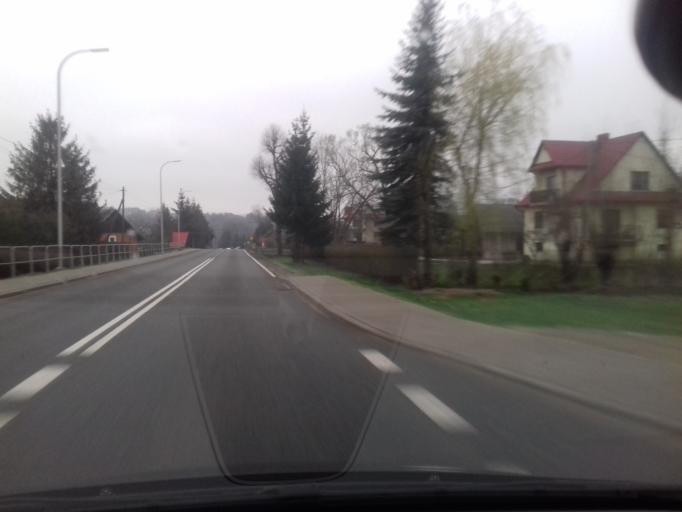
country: PL
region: Lesser Poland Voivodeship
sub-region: Powiat limanowski
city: Tymbark
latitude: 49.7212
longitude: 20.3424
